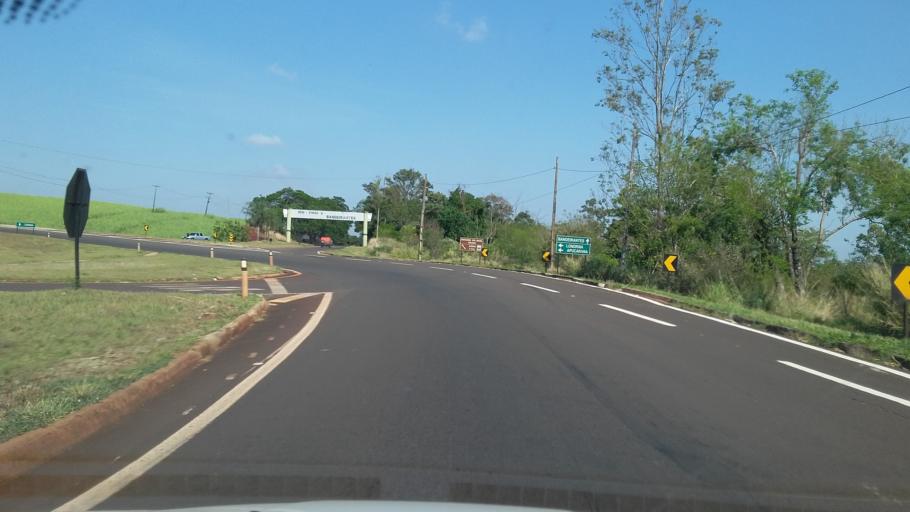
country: BR
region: Parana
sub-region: Bandeirantes
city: Bandeirantes
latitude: -23.1109
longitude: -50.3340
